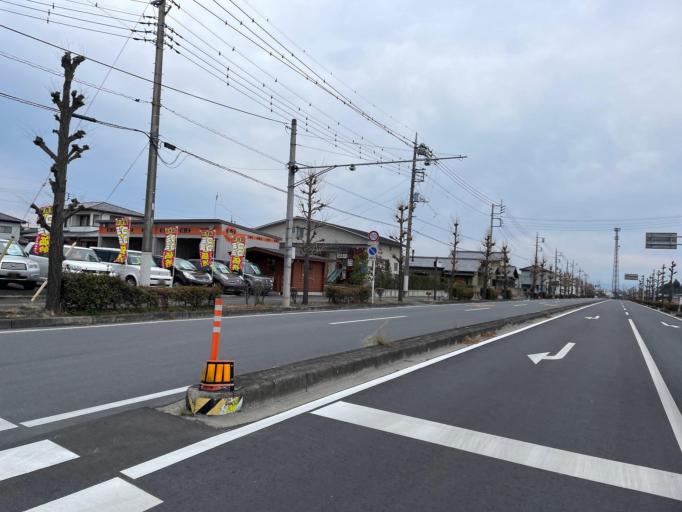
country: JP
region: Gunma
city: Fujioka
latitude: 36.2421
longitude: 139.0856
